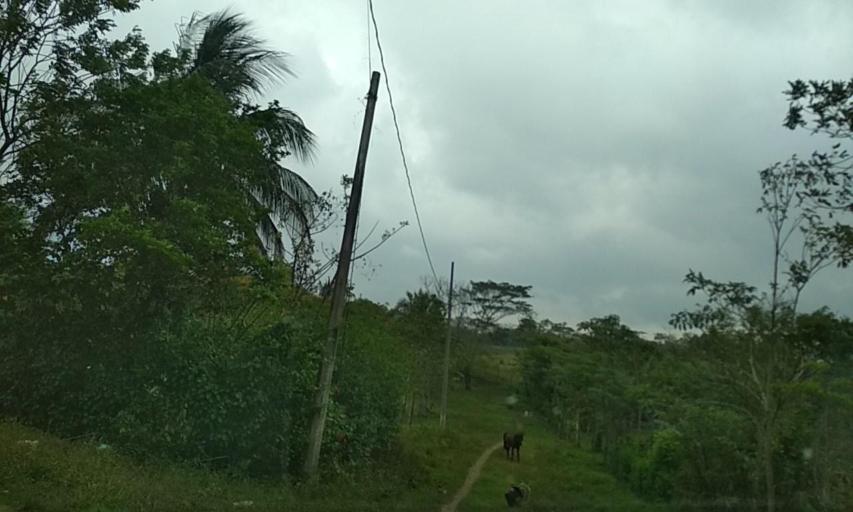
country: MX
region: Tabasco
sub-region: Huimanguillo
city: Francisco Rueda
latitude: 17.6580
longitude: -94.0986
